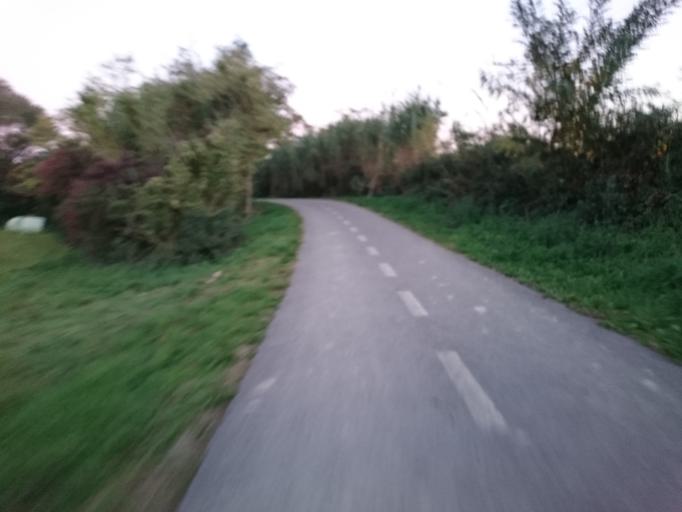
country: SI
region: Koper-Capodistria
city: Pobegi
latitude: 45.5507
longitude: 13.7931
